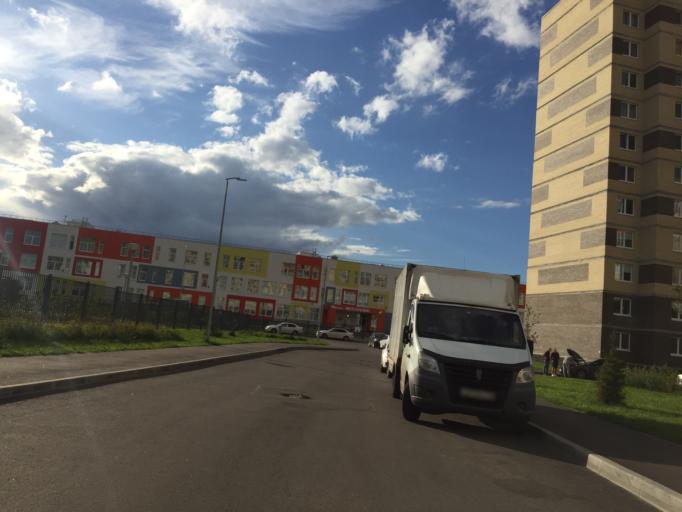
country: RU
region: St.-Petersburg
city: Grazhdanka
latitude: 60.0557
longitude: 30.4181
